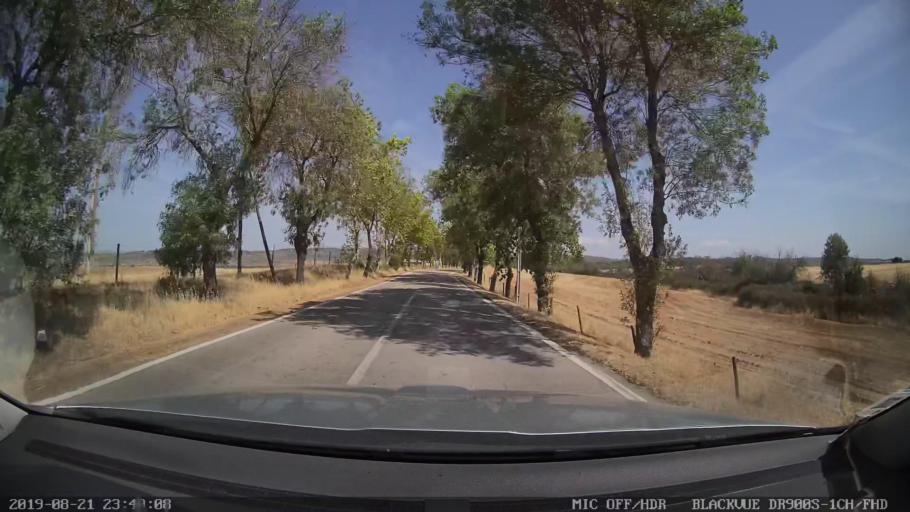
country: PT
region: Castelo Branco
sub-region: Idanha-A-Nova
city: Idanha-a-Nova
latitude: 39.8743
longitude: -7.2517
